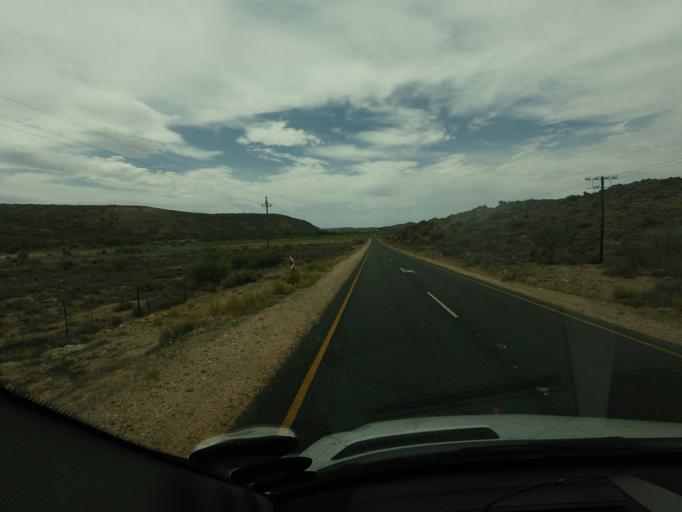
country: ZA
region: Western Cape
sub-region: Overberg District Municipality
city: Swellendam
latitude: -33.8512
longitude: 20.8310
